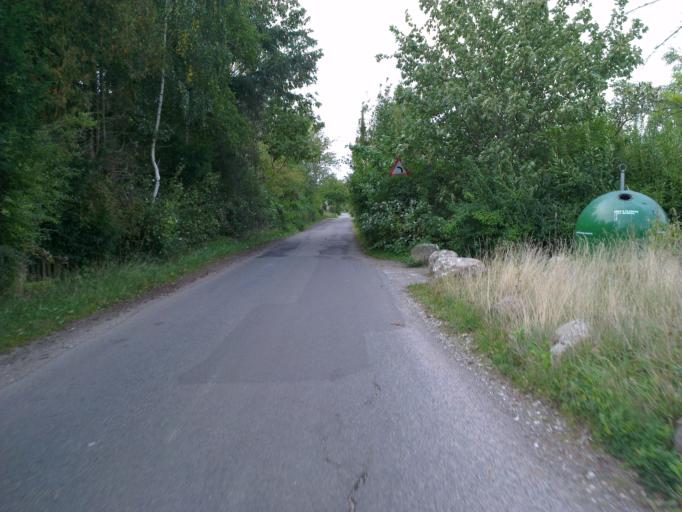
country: DK
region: Capital Region
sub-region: Frederikssund Kommune
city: Jaegerspris
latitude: 55.8338
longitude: 11.9592
